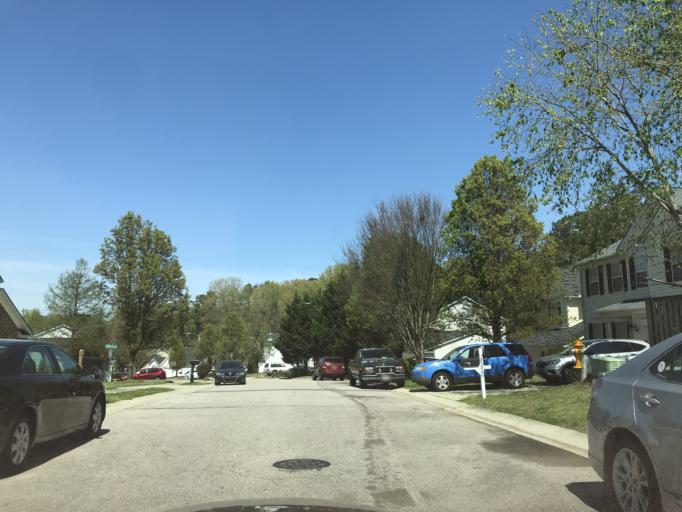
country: US
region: North Carolina
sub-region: Wake County
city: Raleigh
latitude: 35.8130
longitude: -78.5727
